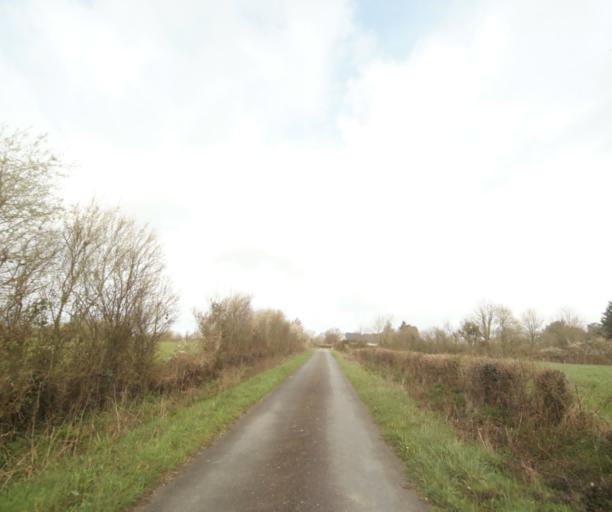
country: FR
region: Pays de la Loire
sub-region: Departement de la Loire-Atlantique
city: Bouvron
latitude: 47.4078
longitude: -1.8720
